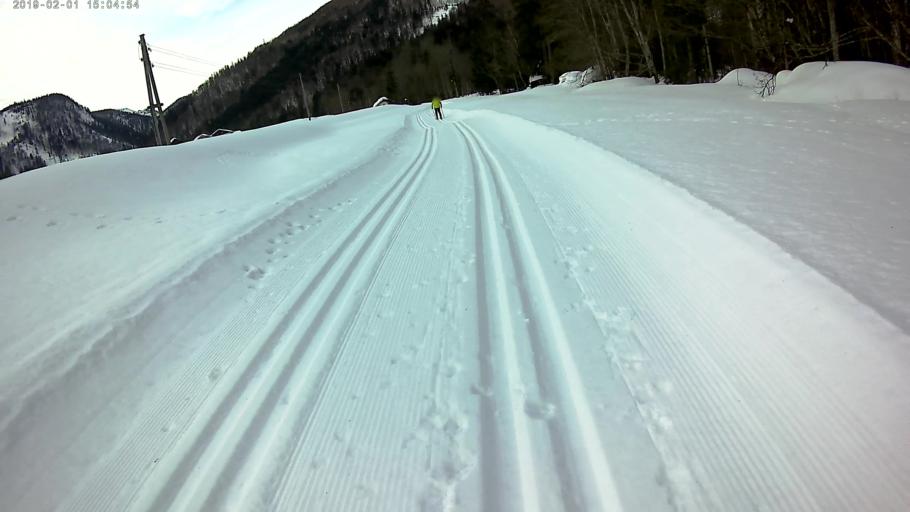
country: AT
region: Salzburg
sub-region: Politischer Bezirk Salzburg-Umgebung
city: Hintersee
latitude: 47.7110
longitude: 13.3058
